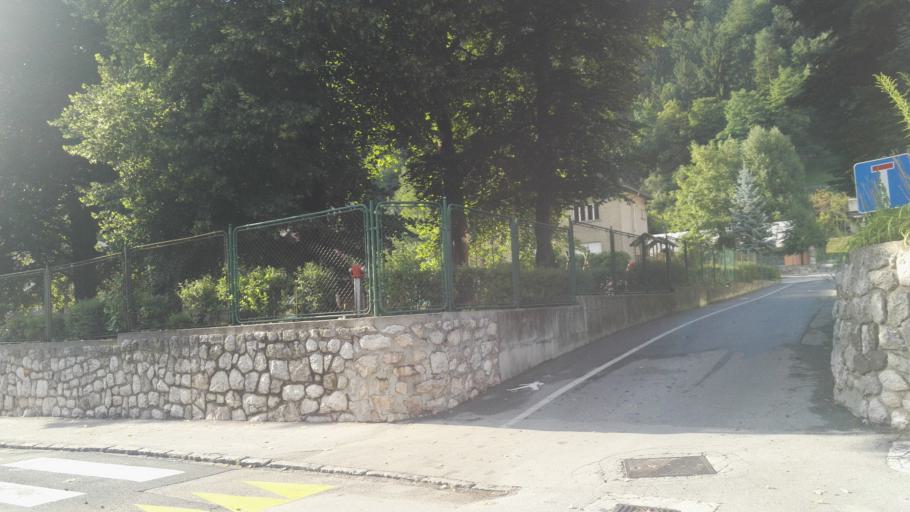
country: SI
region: Jesenice
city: Jesenice
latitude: 46.4359
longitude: 14.0621
